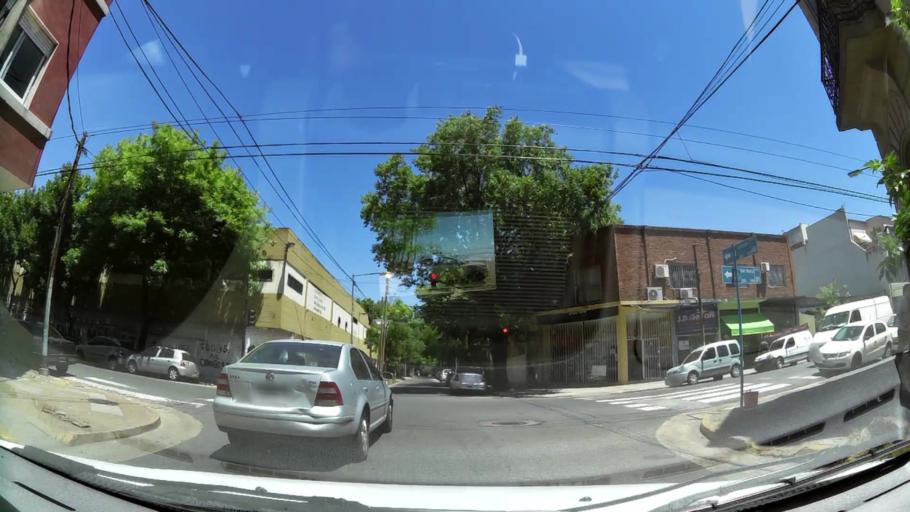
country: AR
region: Buenos Aires
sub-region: Partido de General San Martin
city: General San Martin
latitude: -34.5796
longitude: -58.5354
